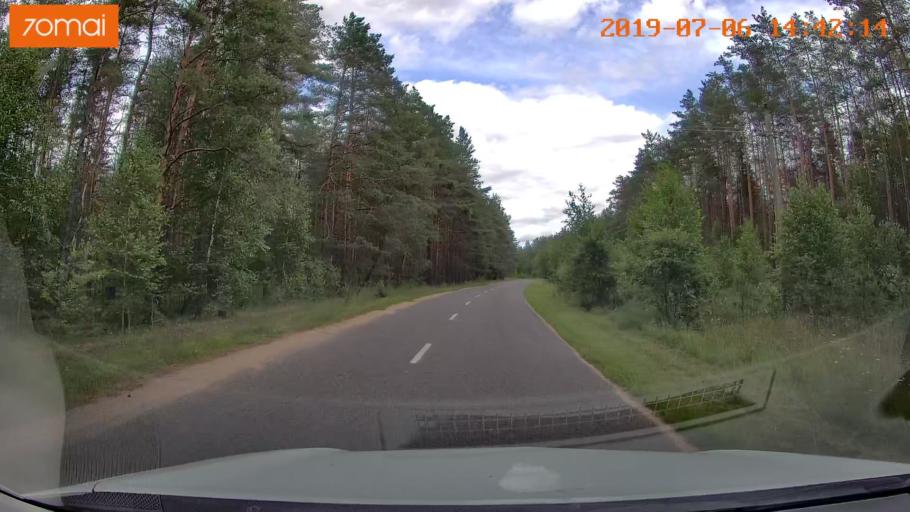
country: BY
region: Minsk
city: Ivyanyets
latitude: 53.9395
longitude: 26.6862
